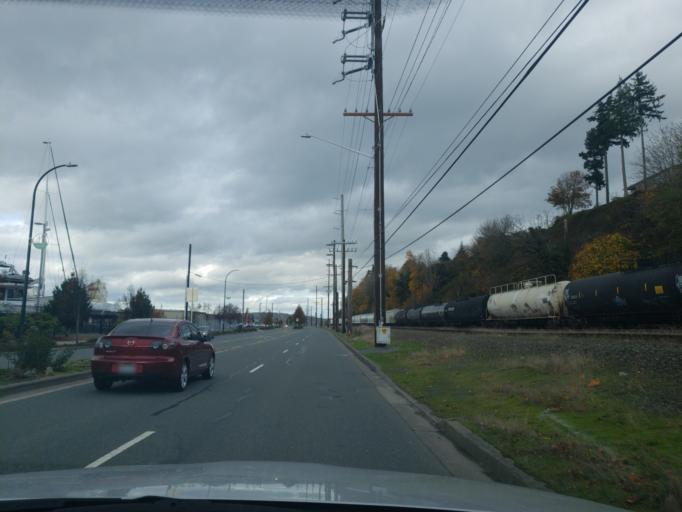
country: US
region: Washington
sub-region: Snohomish County
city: Everett
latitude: 48.0007
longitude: -122.2138
